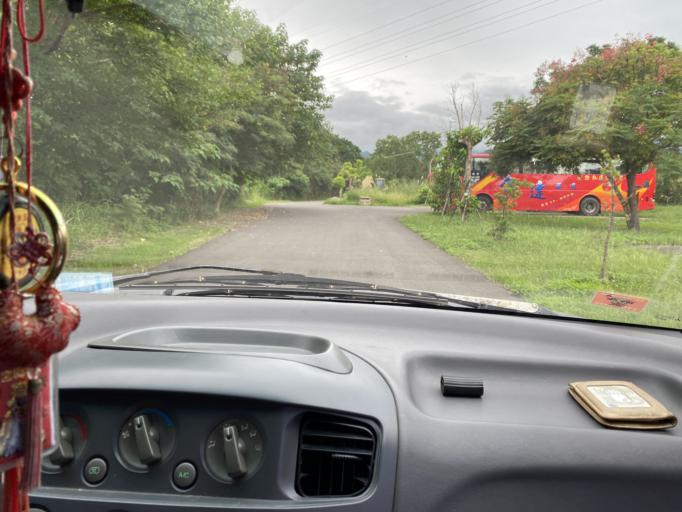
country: TW
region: Taiwan
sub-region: Hsinchu
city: Zhubei
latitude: 24.7196
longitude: 121.1031
